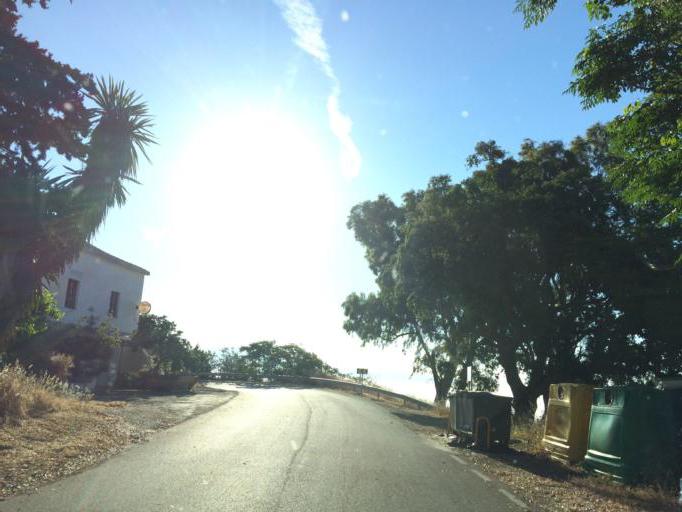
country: ES
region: Andalusia
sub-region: Provincia de Malaga
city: Colmenar
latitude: 36.8397
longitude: -4.3477
